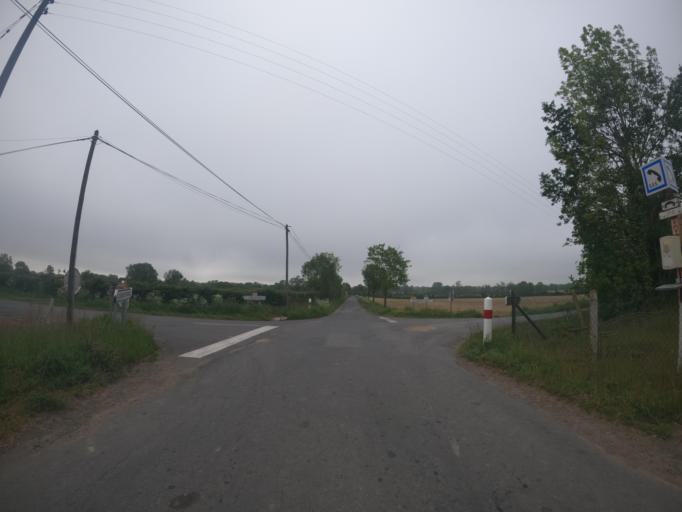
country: FR
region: Poitou-Charentes
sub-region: Departement des Deux-Sevres
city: Chiche
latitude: 46.8952
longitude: -0.3405
